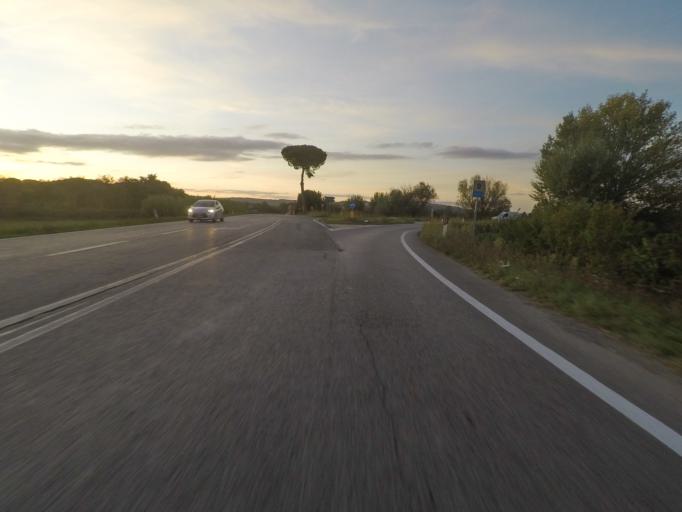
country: IT
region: Tuscany
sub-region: Provincia di Siena
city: Sinalunga
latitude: 43.1895
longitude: 11.7578
